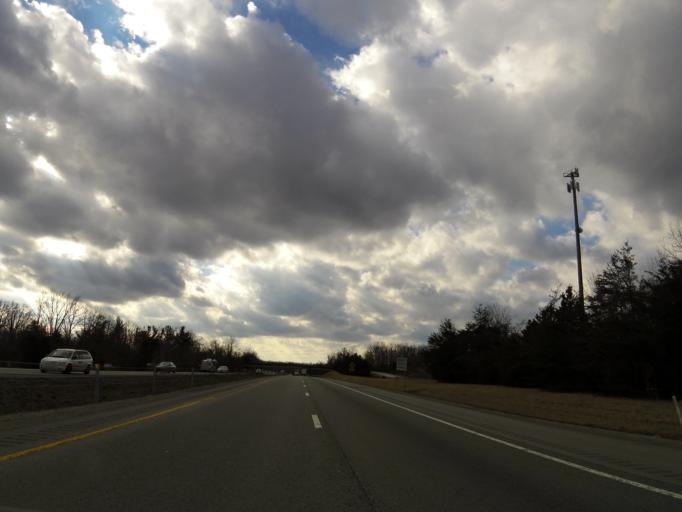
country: US
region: Tennessee
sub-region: Putnam County
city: Monterey
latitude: 36.1359
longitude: -85.3203
